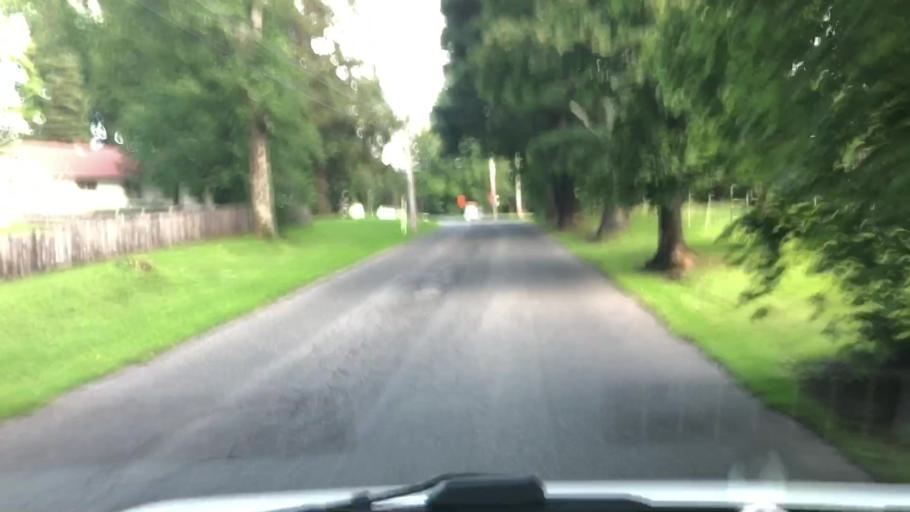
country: US
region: Massachusetts
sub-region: Berkshire County
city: Lee
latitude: 42.3018
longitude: -73.2643
